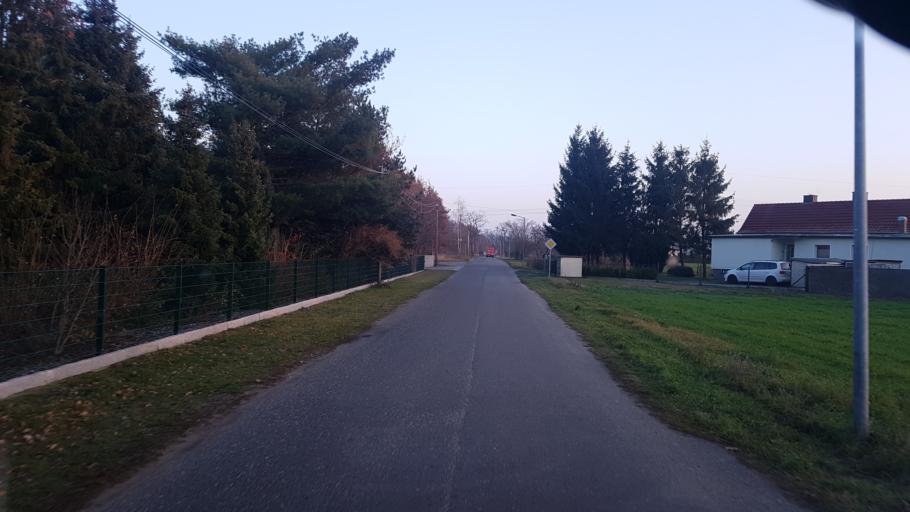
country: DE
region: Brandenburg
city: Tettau
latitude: 51.4777
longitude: 13.7199
